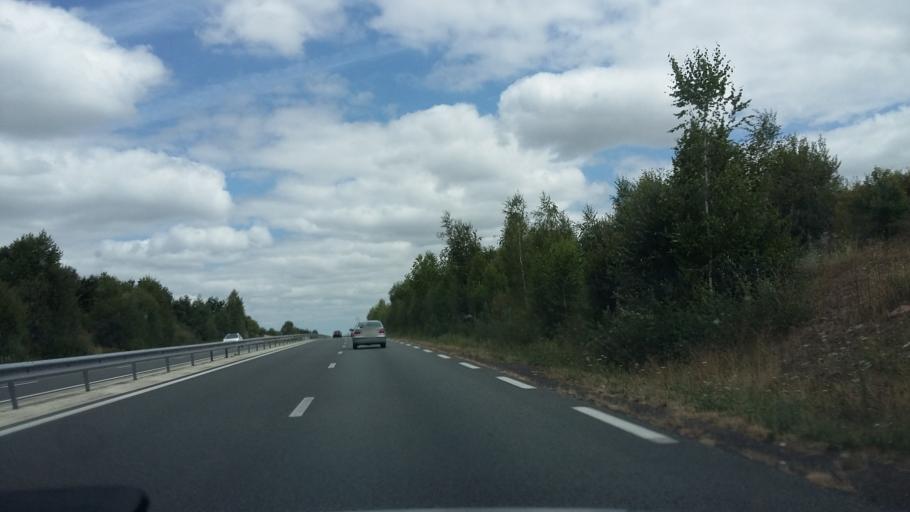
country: FR
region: Pays de la Loire
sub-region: Departement de la Vendee
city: La Chaize-le-Vicomte
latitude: 46.6655
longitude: -1.2944
